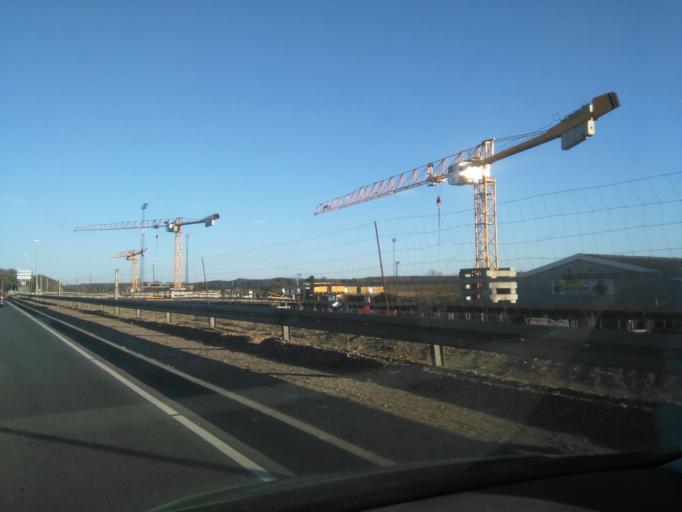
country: DK
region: Central Jutland
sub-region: Silkeborg Kommune
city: Silkeborg
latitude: 56.1821
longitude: 9.5859
